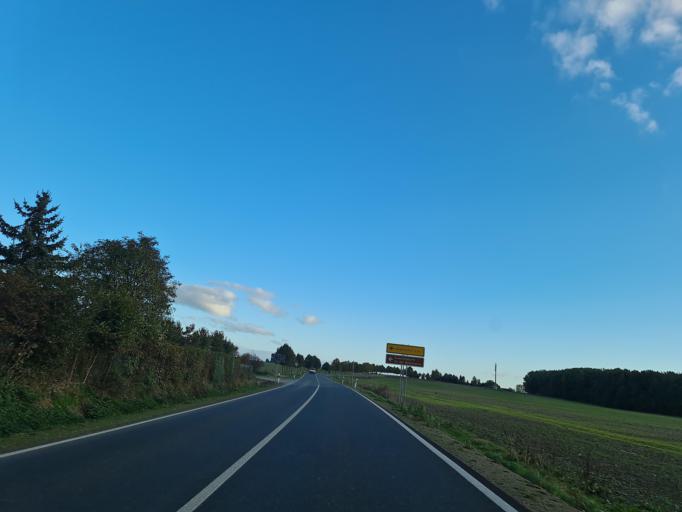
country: DE
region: Thuringia
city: Wildetaube
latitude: 50.7275
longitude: 12.1059
